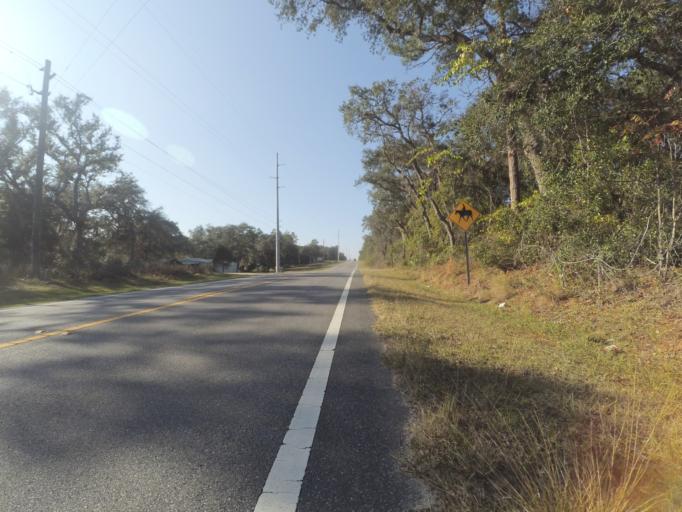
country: US
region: Florida
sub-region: Lake County
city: Umatilla
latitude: 28.9755
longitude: -81.6895
